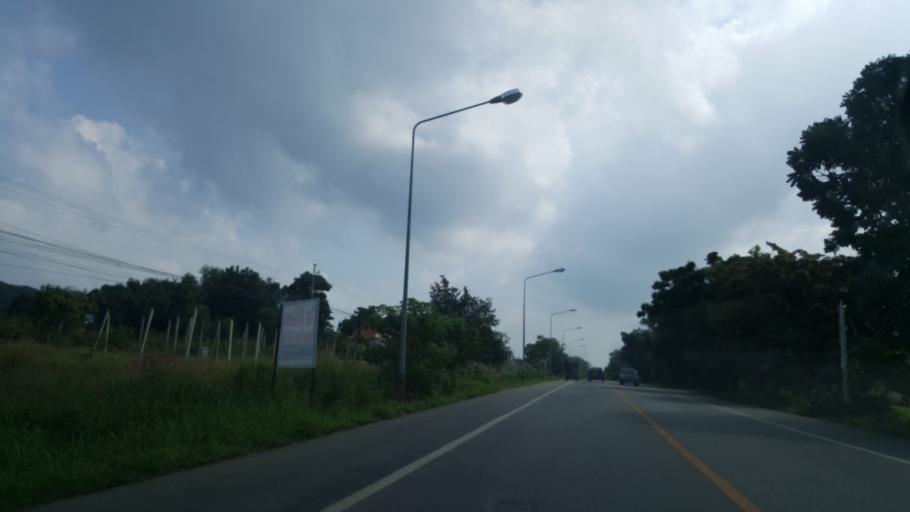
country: TH
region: Chon Buri
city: Sattahip
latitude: 12.7317
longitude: 100.9124
